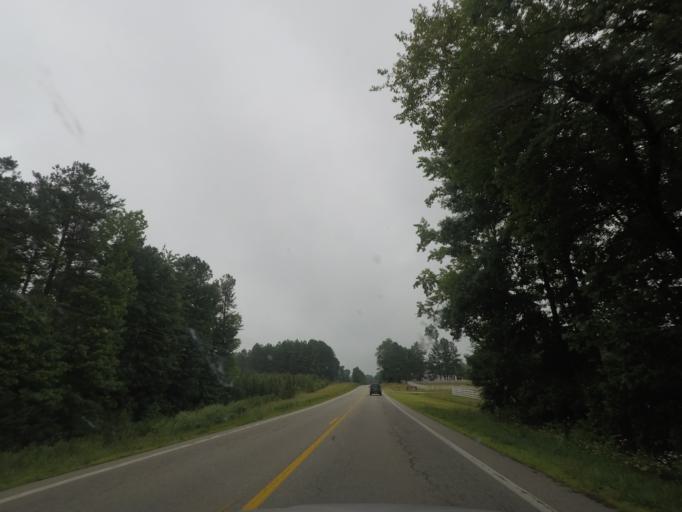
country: US
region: Virginia
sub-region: Prince Edward County
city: Hampden Sydney
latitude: 37.0905
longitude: -78.4744
